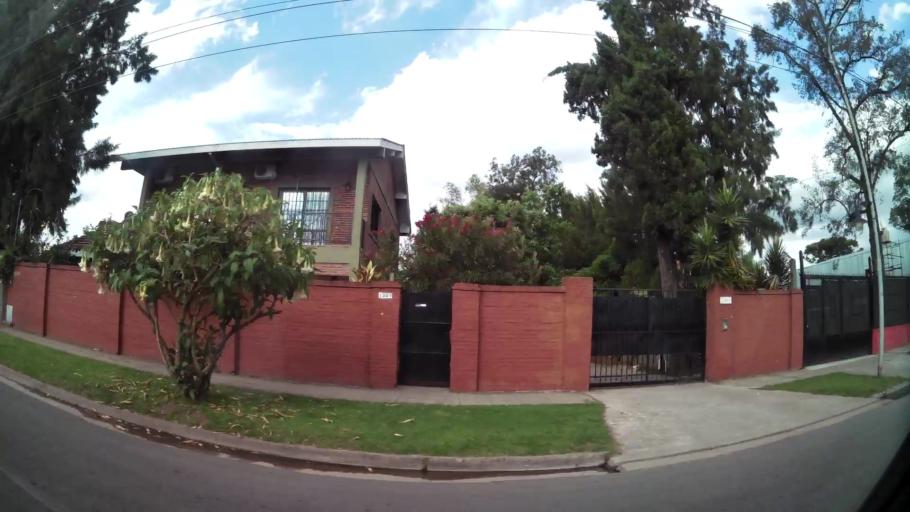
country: AR
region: Buenos Aires
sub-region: Partido de Tigre
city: Tigre
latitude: -34.4699
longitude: -58.6551
